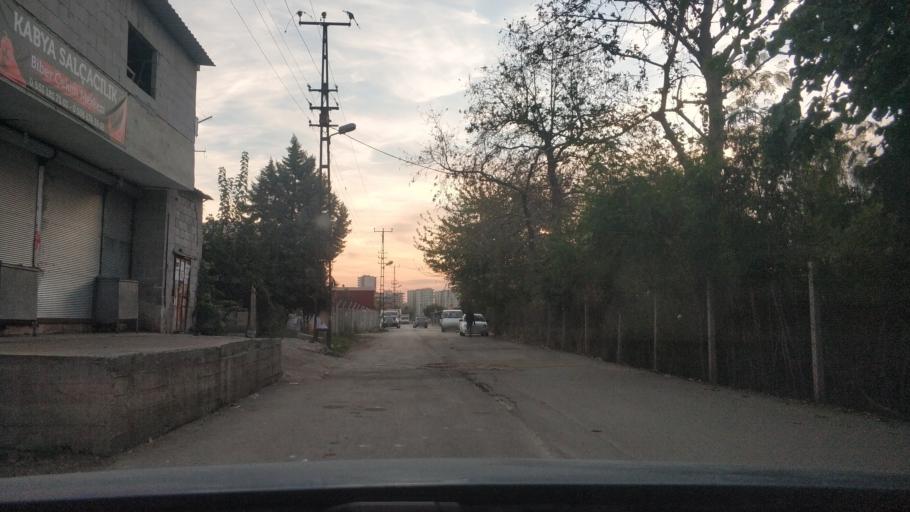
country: TR
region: Adana
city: Seyhan
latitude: 37.0116
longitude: 35.2954
